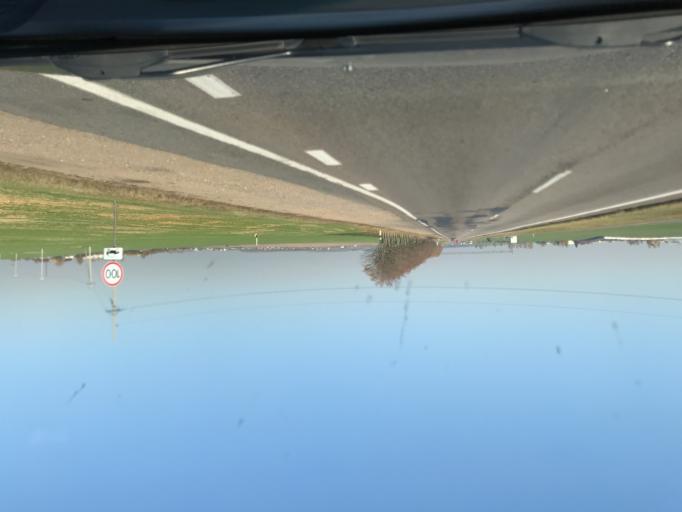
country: BY
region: Minsk
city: Luhavaya Slabada
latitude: 53.7367
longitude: 27.8469
